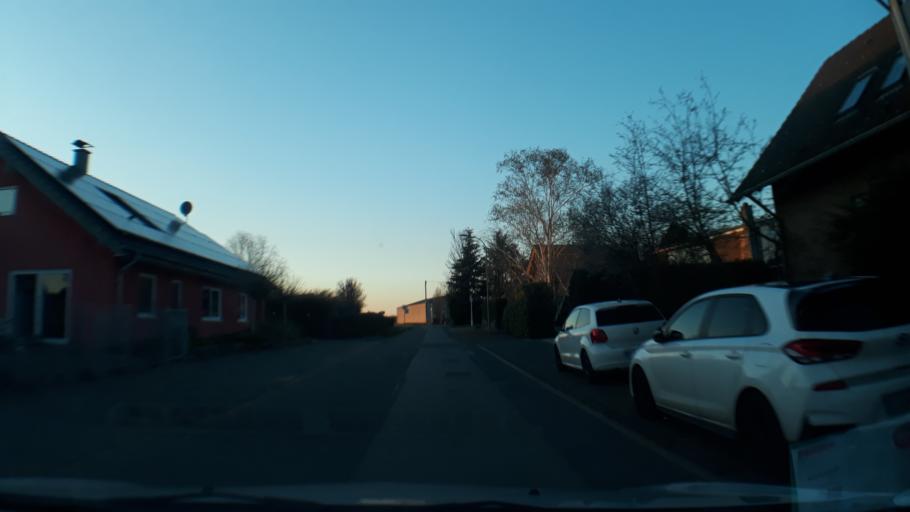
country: DE
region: North Rhine-Westphalia
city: Zulpich
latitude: 50.7043
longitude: 6.6202
